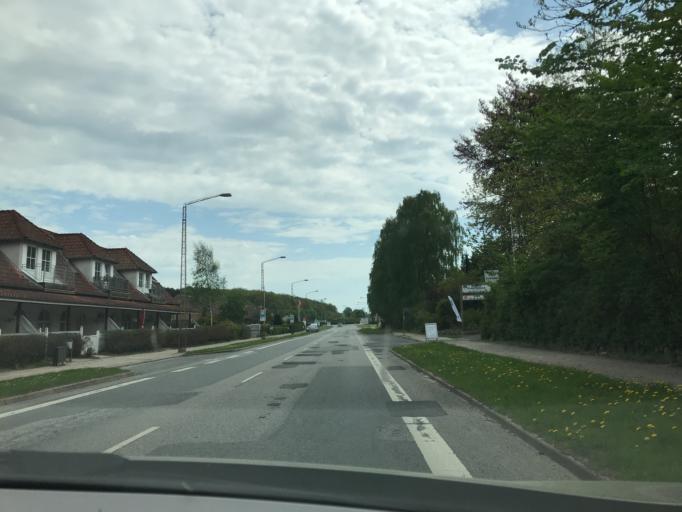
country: DK
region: South Denmark
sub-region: Assens Kommune
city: Assens
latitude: 55.2628
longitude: 9.9082
